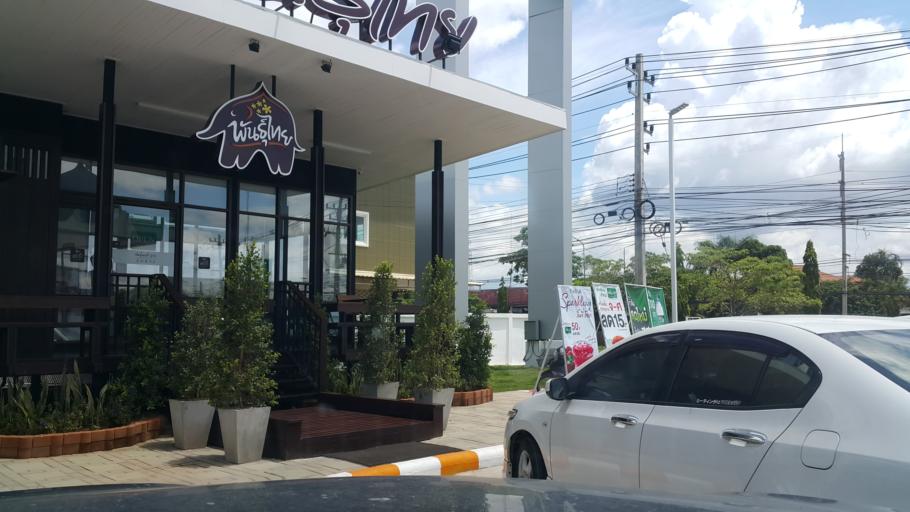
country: TH
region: Phayao
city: Phayao
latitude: 19.1960
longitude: 99.8756
